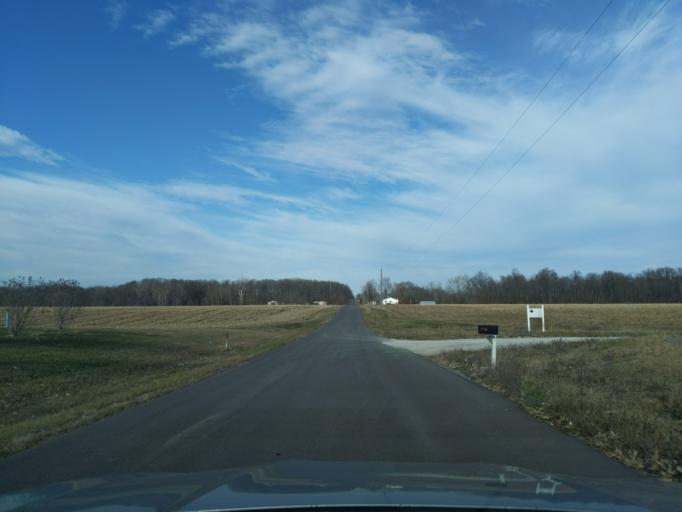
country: US
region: Indiana
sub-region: Decatur County
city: Greensburg
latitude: 39.2226
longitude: -85.4295
